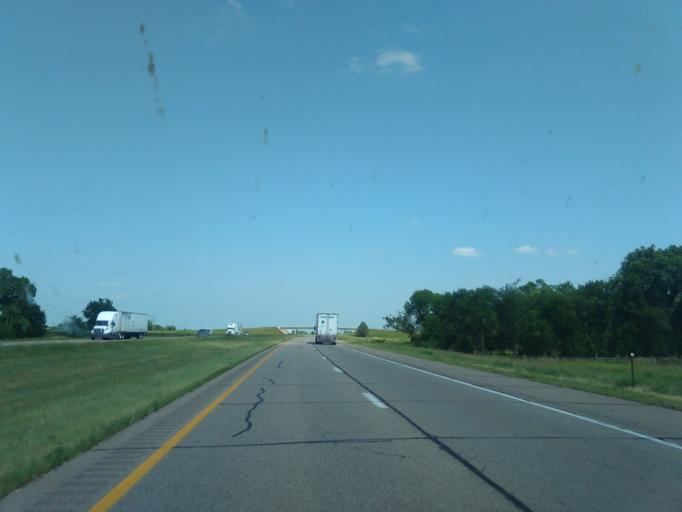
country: US
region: Nebraska
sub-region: Phelps County
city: Holdrege
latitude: 40.6909
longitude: -99.3483
